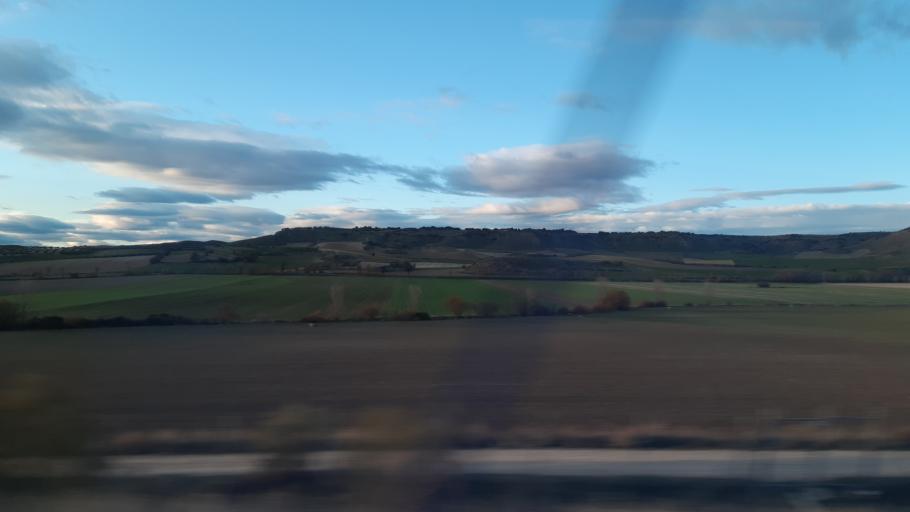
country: ES
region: Madrid
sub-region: Provincia de Madrid
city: Villalbilla
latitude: 40.4592
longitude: -3.3055
